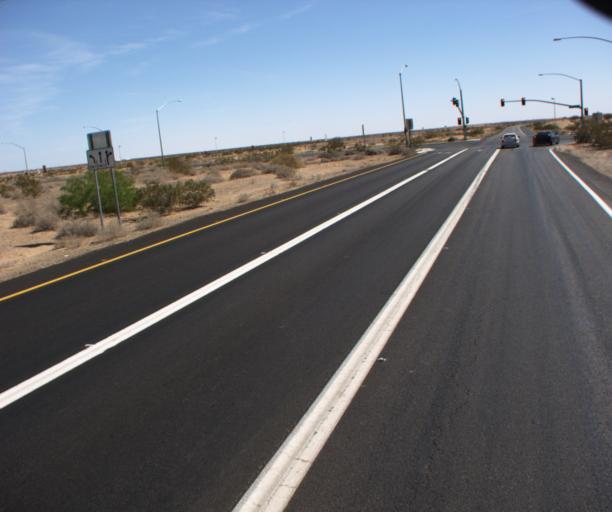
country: US
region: Arizona
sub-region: Yuma County
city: Fortuna Foothills
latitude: 32.6274
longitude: -114.5214
